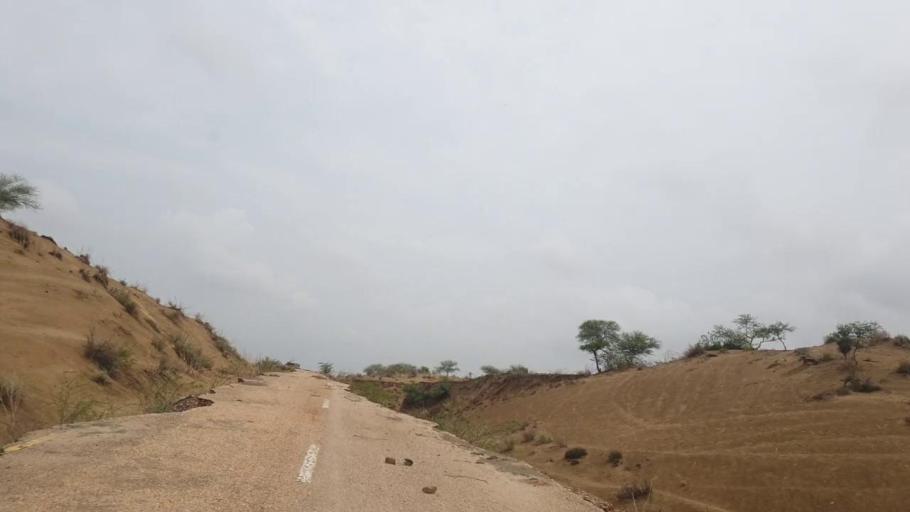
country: PK
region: Sindh
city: Naukot
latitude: 24.6317
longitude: 69.3545
